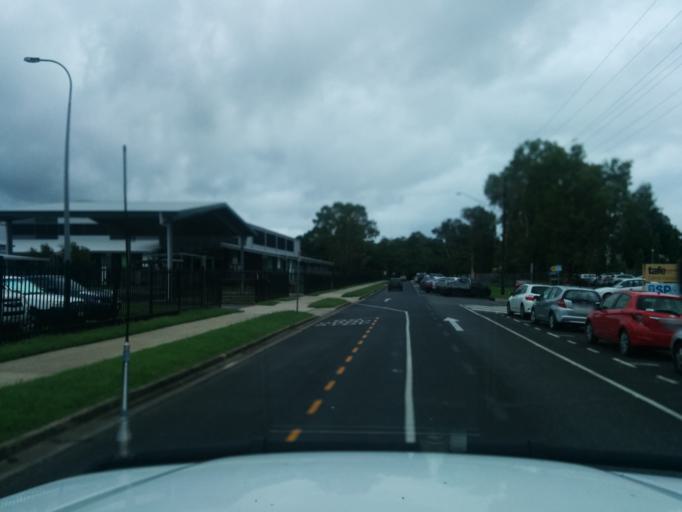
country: AU
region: Queensland
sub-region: Cairns
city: Cairns
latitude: -16.9219
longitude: 145.7536
